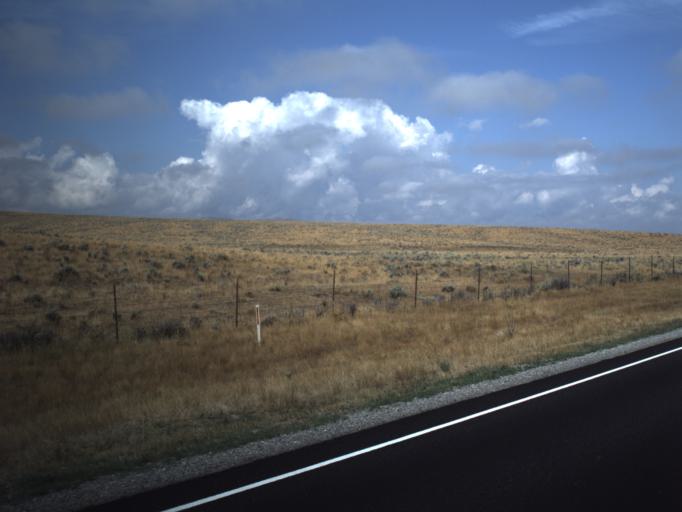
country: US
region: Utah
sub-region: Rich County
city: Randolph
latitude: 41.5546
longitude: -111.1551
